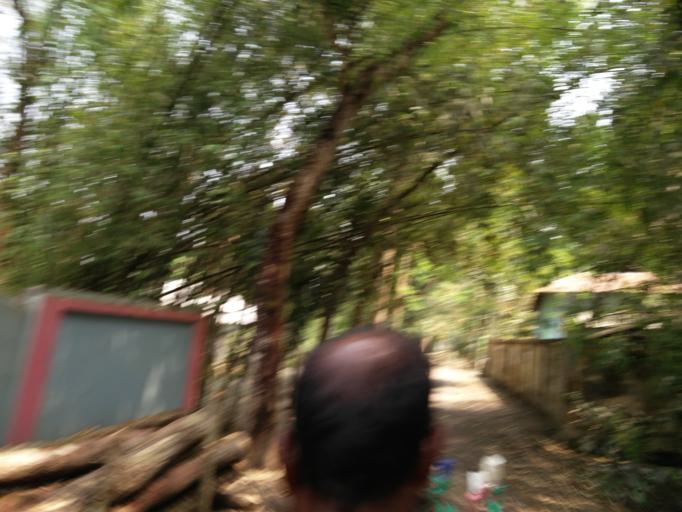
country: BD
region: Dhaka
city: Sherpur
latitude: 24.9337
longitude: 90.1651
